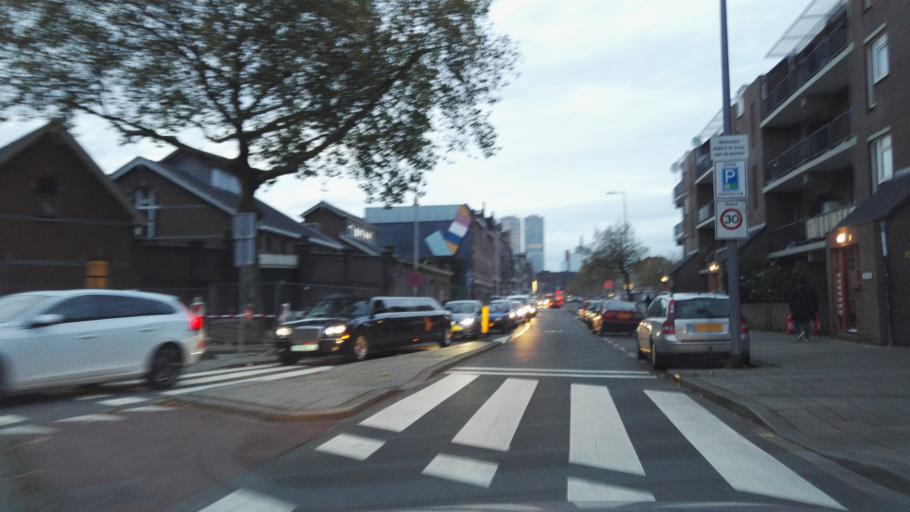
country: NL
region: South Holland
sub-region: Gemeente Rotterdam
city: Rotterdam
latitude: 51.8984
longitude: 4.5014
